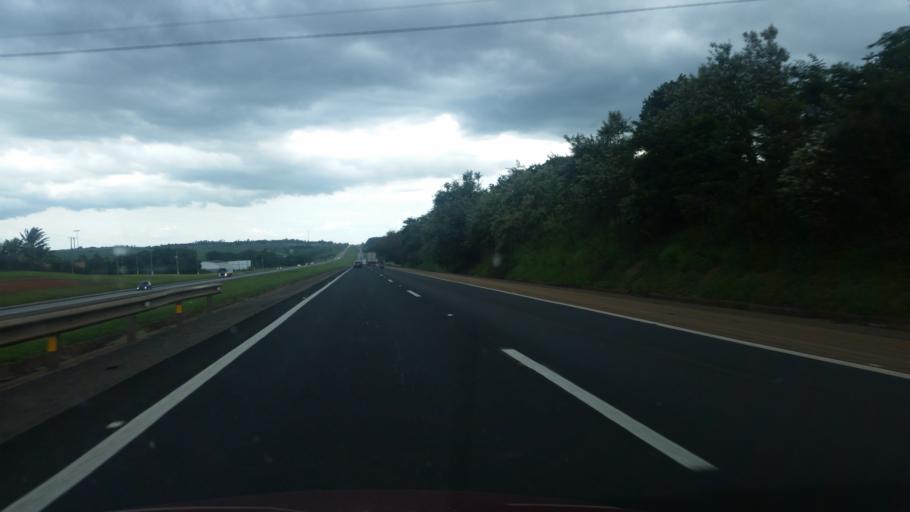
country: BR
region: Sao Paulo
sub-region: Boituva
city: Boituva
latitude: -23.3228
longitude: -47.5752
